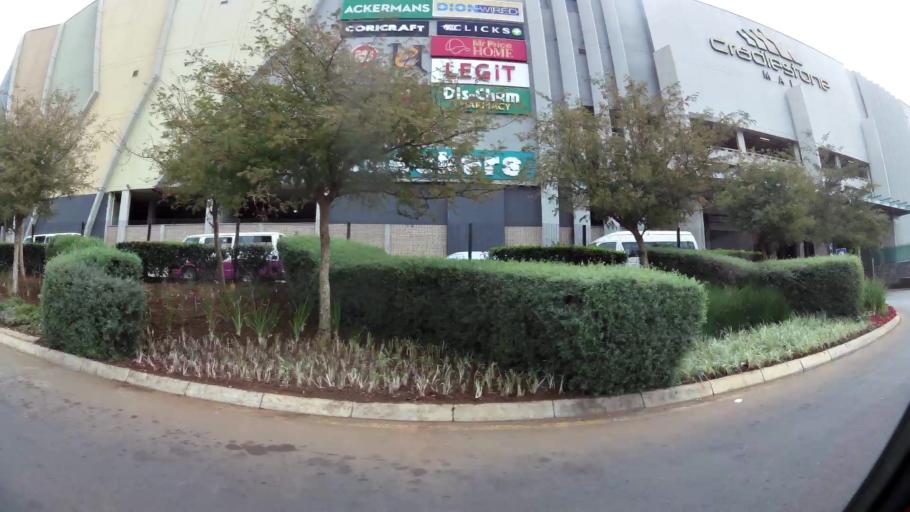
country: ZA
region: Gauteng
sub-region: West Rand District Municipality
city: Muldersdriseloop
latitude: -26.0618
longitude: 27.8391
